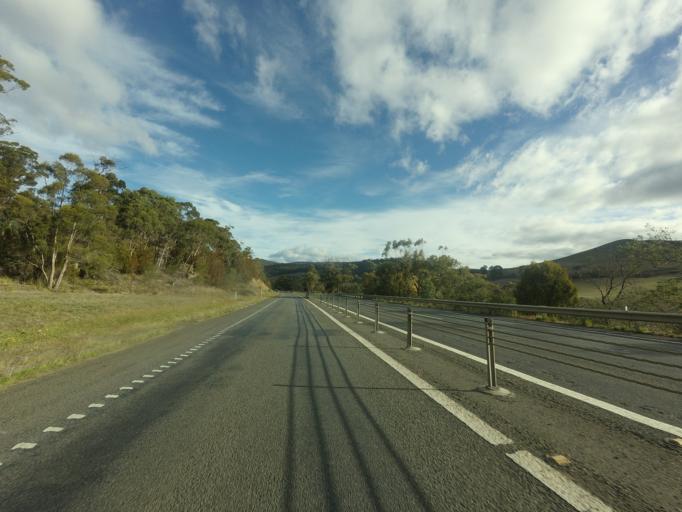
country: AU
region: Tasmania
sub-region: Brighton
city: Bridgewater
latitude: -42.5852
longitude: 147.2265
